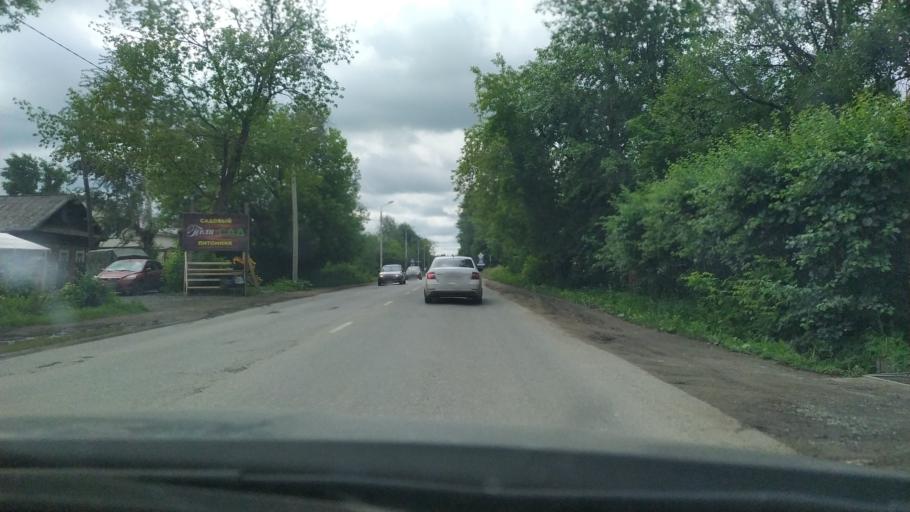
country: RU
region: Perm
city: Perm
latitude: 57.9805
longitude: 56.3050
